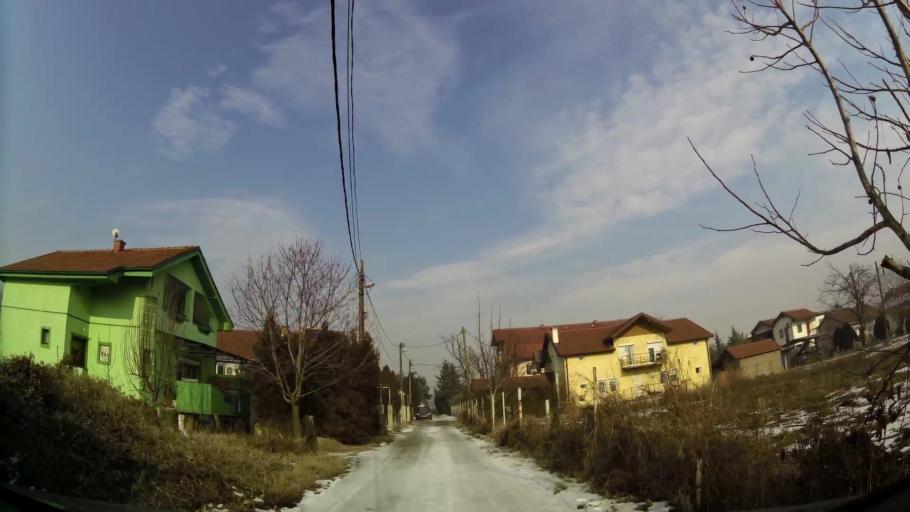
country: MK
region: Ilinden
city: Jurumleri
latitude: 41.9948
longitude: 21.5182
